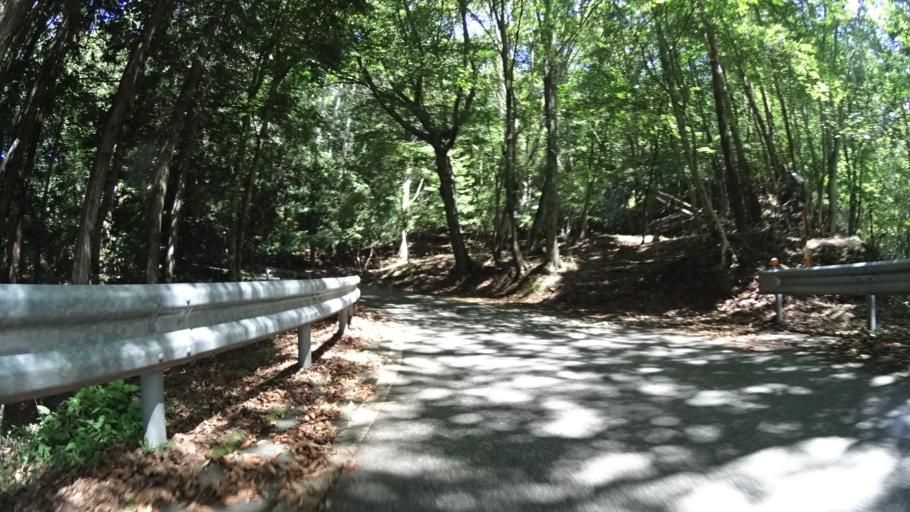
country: JP
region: Yamanashi
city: Enzan
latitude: 35.7426
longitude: 138.8180
